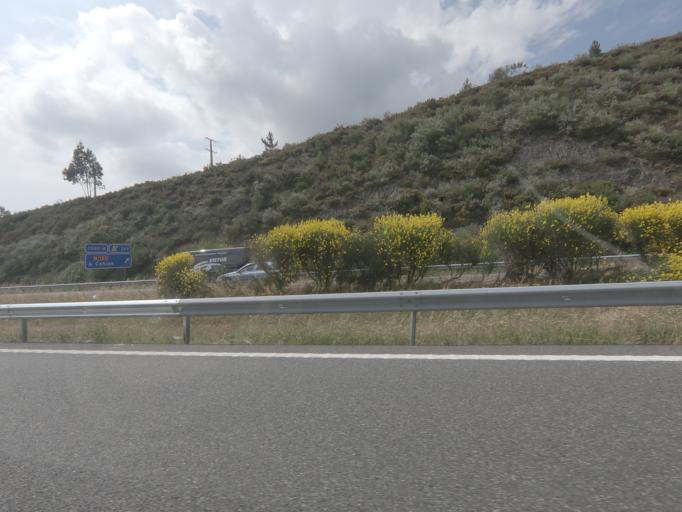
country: ES
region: Galicia
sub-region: Provincia de Ourense
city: Melon
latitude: 42.2236
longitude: -8.2442
